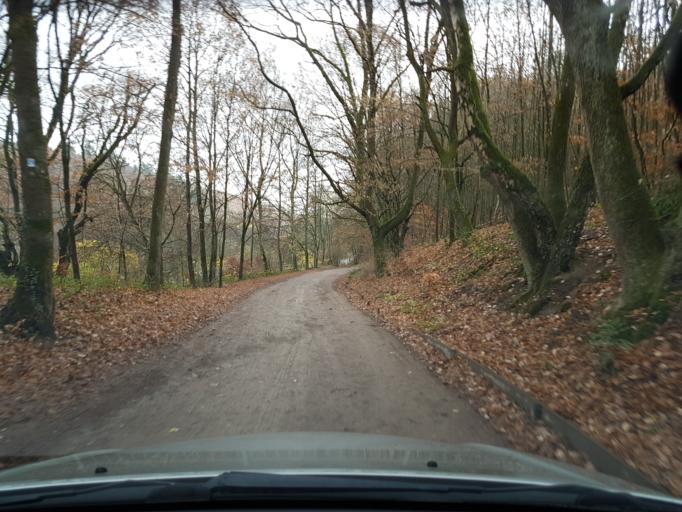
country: DE
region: Hesse
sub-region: Regierungsbezirk Darmstadt
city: Kiedrich
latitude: 50.0419
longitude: 8.0461
